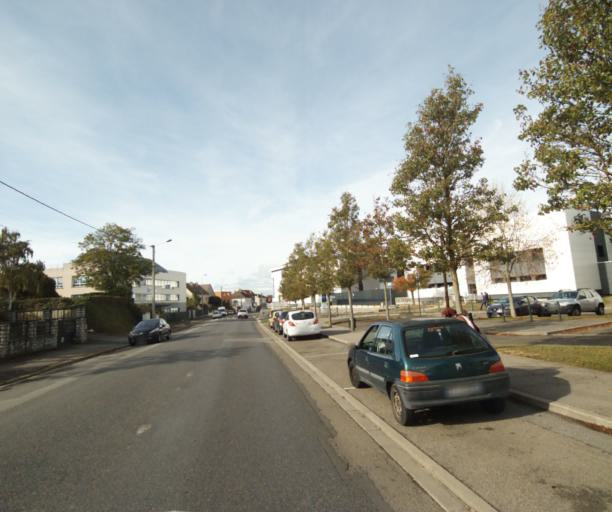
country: FR
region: Centre
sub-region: Departement d'Eure-et-Loir
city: Dreux
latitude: 48.7305
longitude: 1.3790
